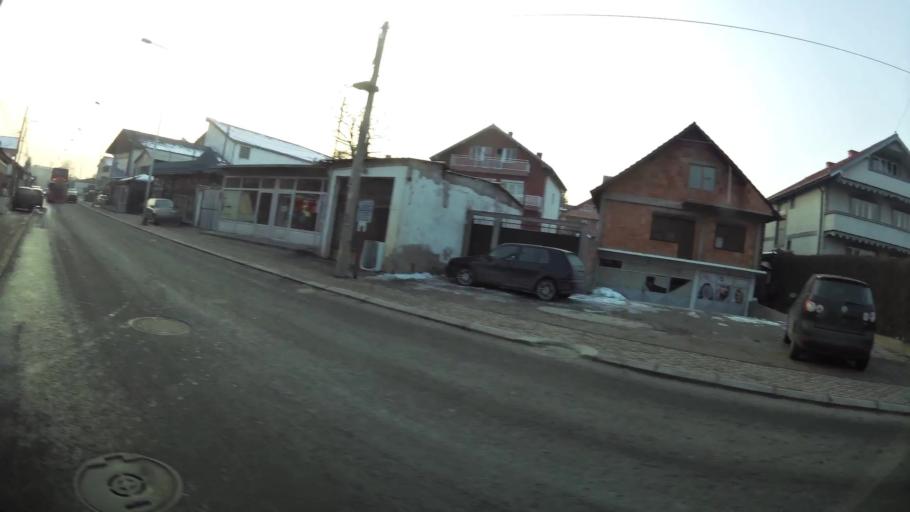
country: MK
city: Creshevo
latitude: 42.0147
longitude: 21.5112
